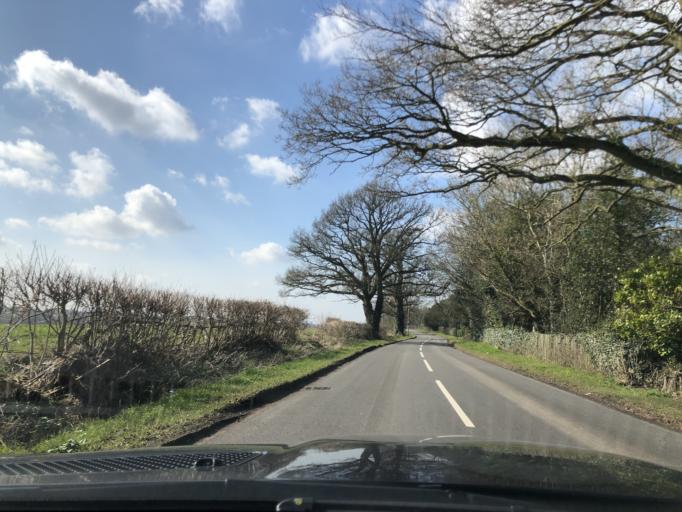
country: GB
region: England
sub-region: Warwickshire
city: Harbury
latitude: 52.2865
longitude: -1.4701
